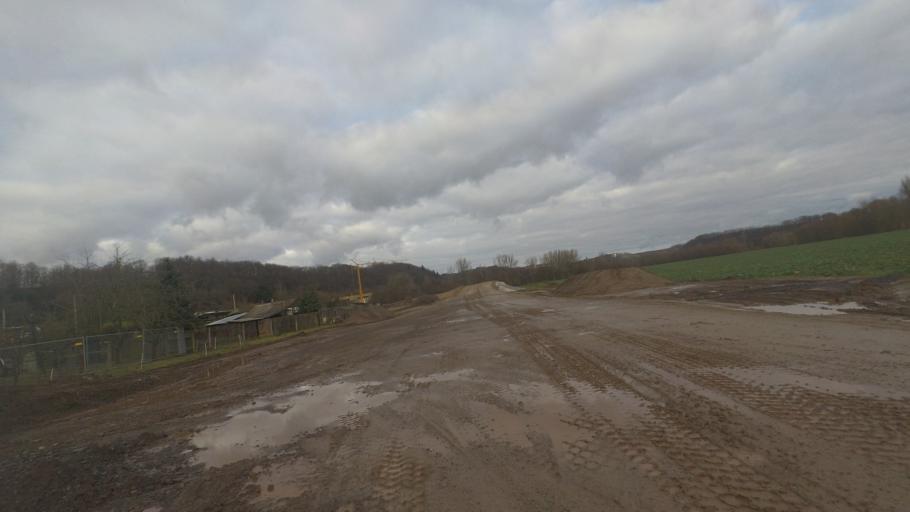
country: DE
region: Thuringia
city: Orlamunde
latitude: 50.7548
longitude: 11.5092
